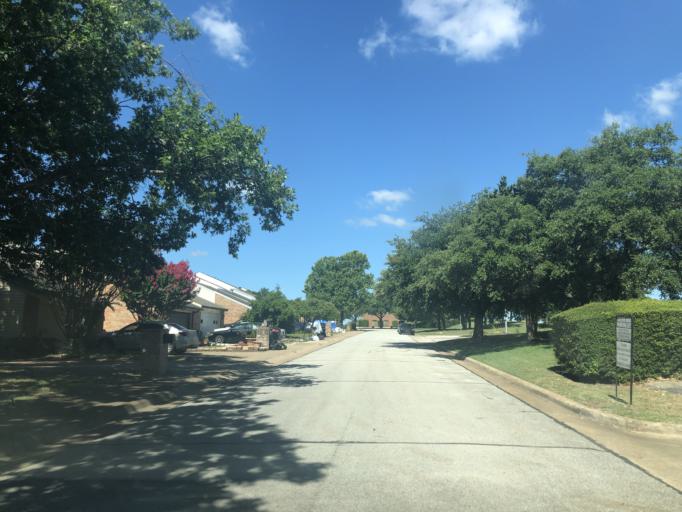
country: US
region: Texas
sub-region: Dallas County
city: Duncanville
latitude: 32.6467
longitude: -96.9398
